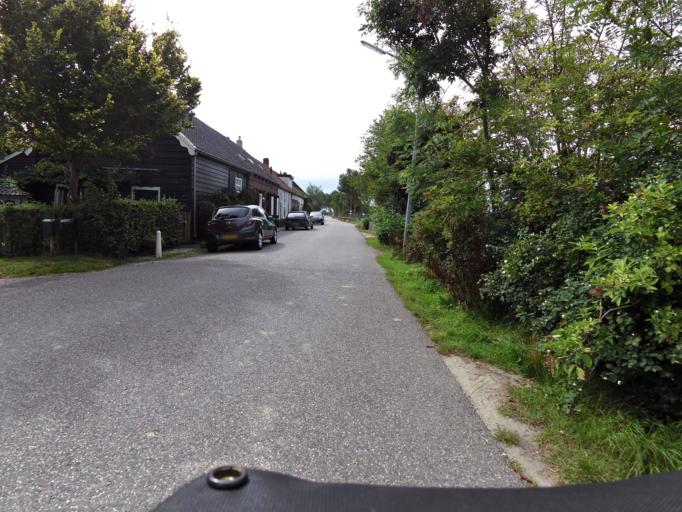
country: NL
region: South Holland
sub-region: Gemeente Goeree-Overflakkee
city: Middelharnis
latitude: 51.7159
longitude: 4.1562
